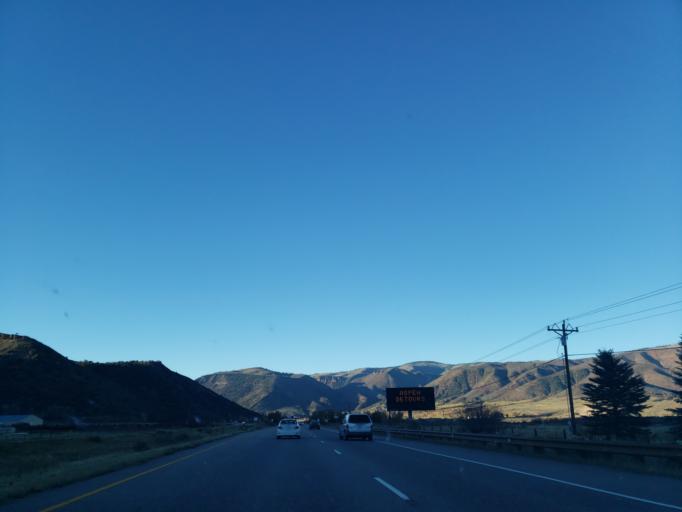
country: US
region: Colorado
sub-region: Pitkin County
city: Snowmass Village
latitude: 39.2559
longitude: -106.8859
